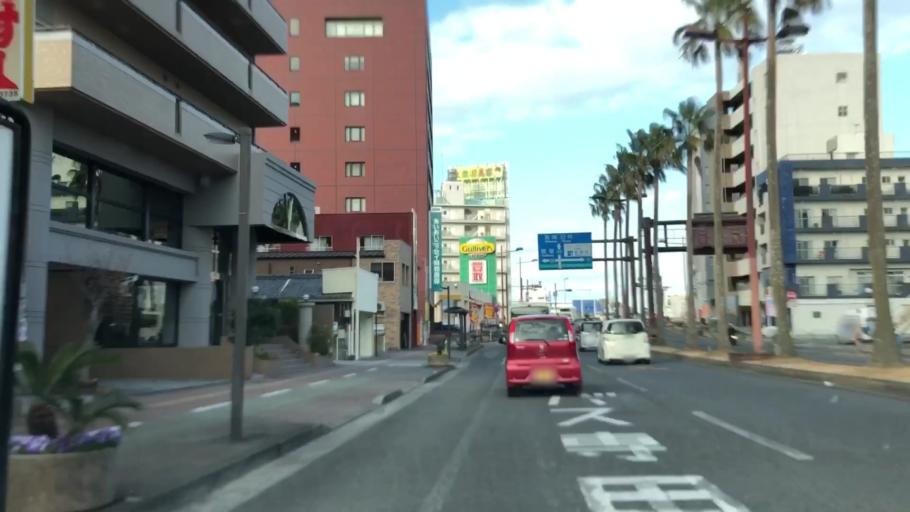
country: JP
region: Miyazaki
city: Miyazaki-shi
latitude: 31.9025
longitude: 131.4190
